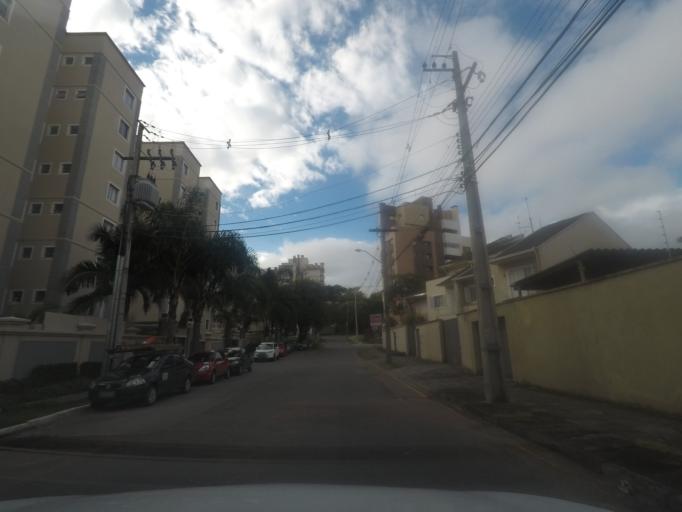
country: BR
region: Parana
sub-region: Curitiba
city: Curitiba
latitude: -25.4341
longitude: -49.2421
